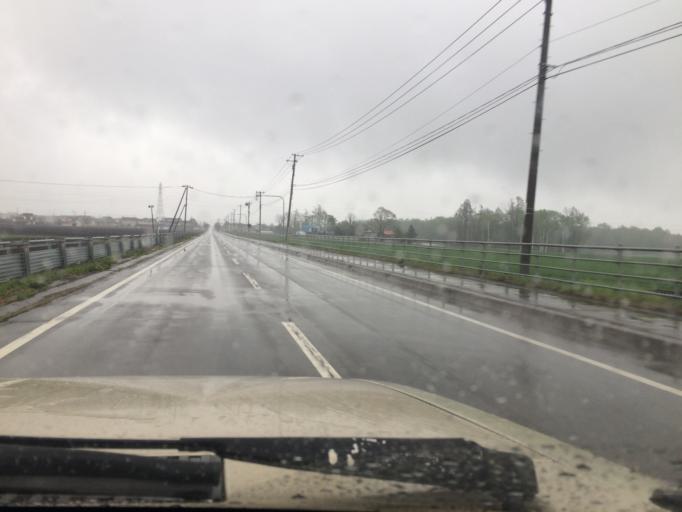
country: JP
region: Hokkaido
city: Obihiro
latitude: 42.8942
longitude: 143.0423
